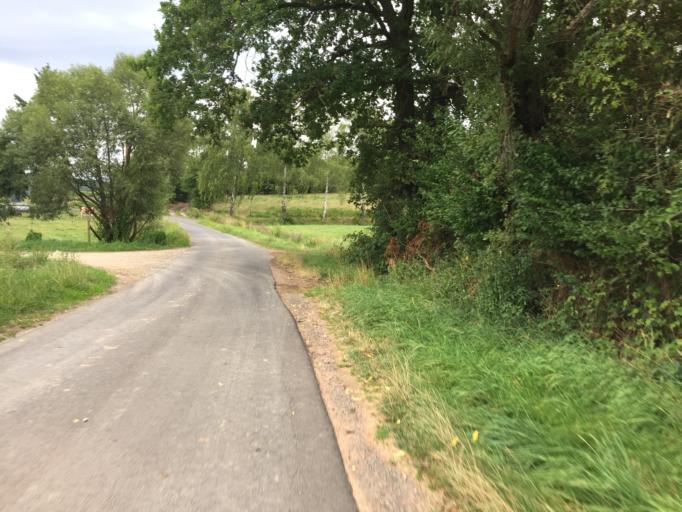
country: DE
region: Hesse
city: Breitenbach
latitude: 50.9247
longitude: 9.7896
